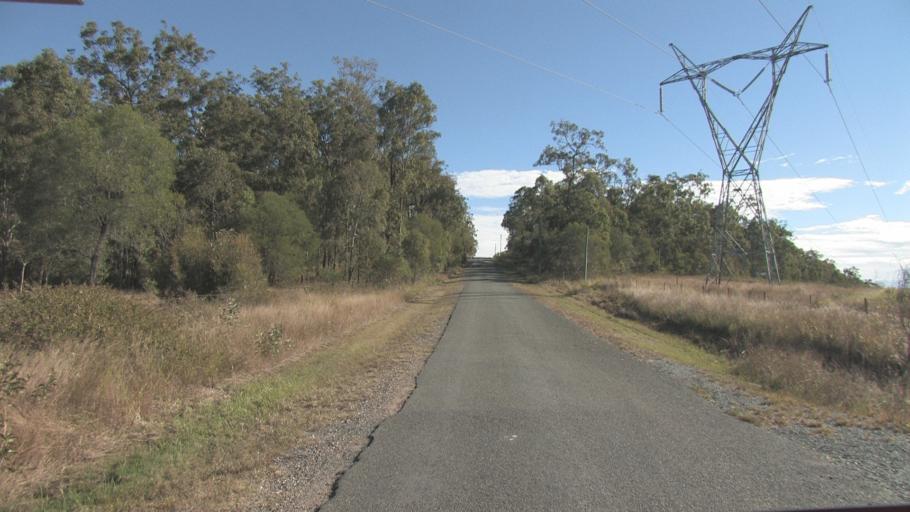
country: AU
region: Queensland
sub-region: Logan
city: Chambers Flat
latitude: -27.7970
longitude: 153.0832
